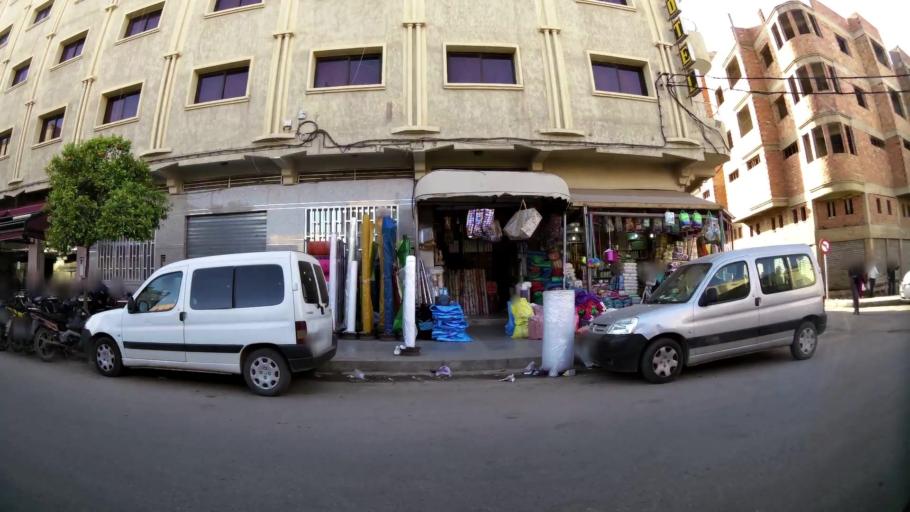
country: MA
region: Oriental
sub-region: Oujda-Angad
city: Oujda
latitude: 34.6781
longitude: -1.9105
